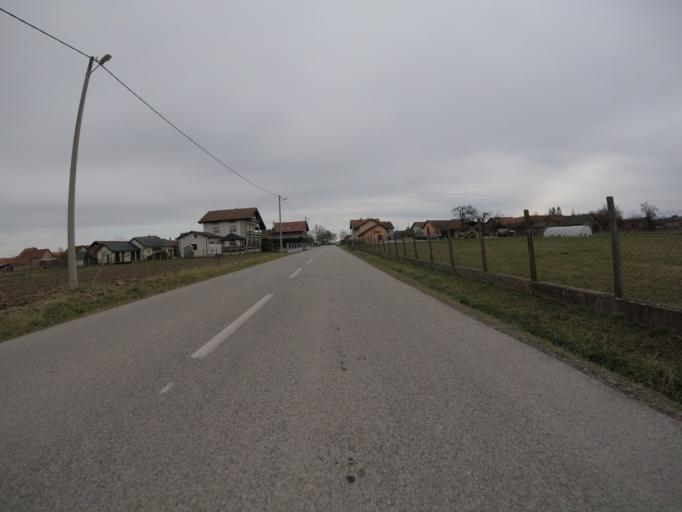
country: HR
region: Grad Zagreb
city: Strmec
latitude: 45.6658
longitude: 15.9363
